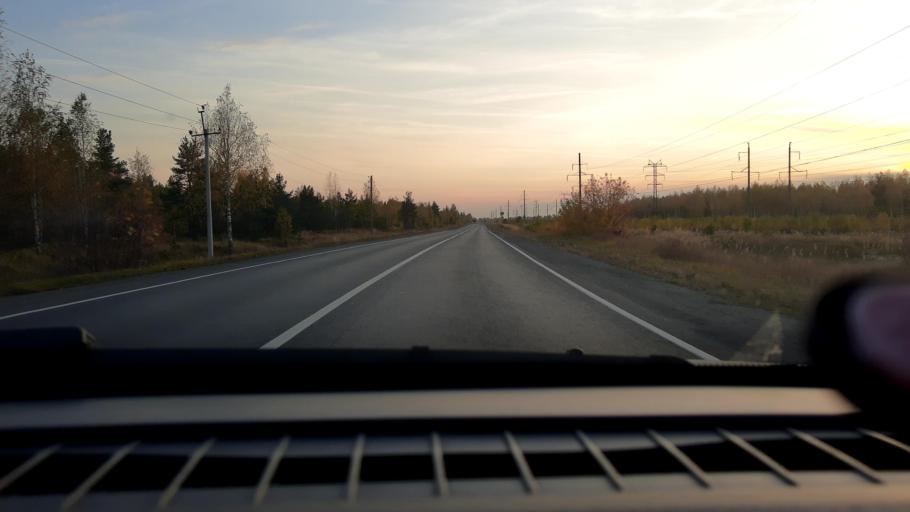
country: RU
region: Nizjnij Novgorod
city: Lukino
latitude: 56.3370
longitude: 43.5772
